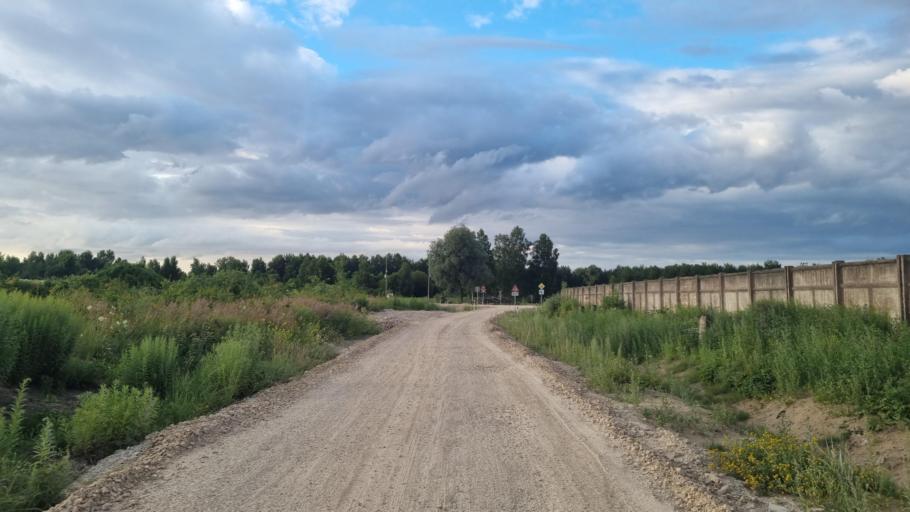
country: LV
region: Stopini
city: Ulbroka
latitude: 56.9171
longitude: 24.2397
